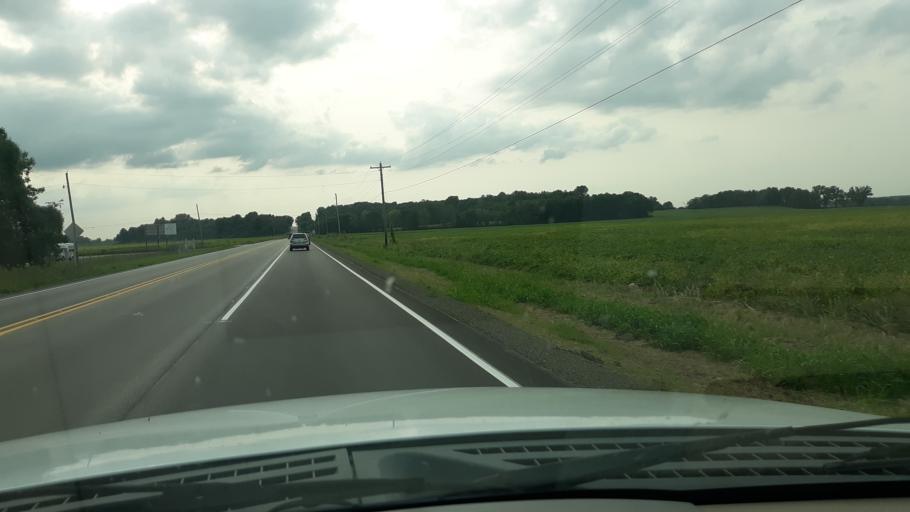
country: US
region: Indiana
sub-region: Gibson County
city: Princeton
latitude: 38.3558
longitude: -87.6426
